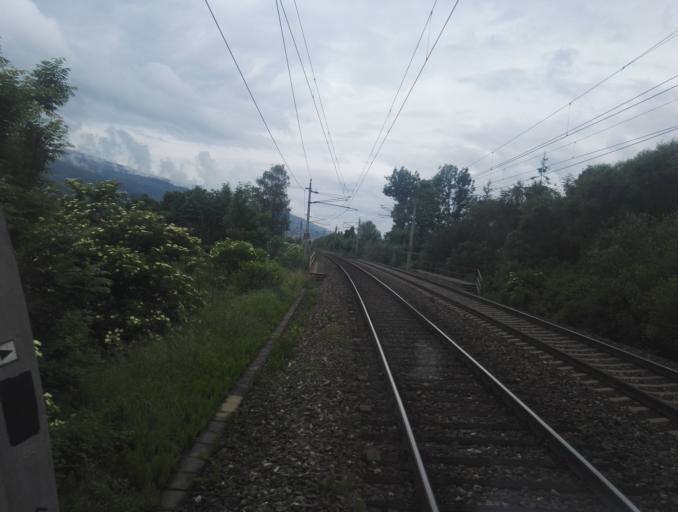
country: AT
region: Styria
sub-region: Politischer Bezirk Bruck-Muerzzuschlag
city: Mitterdorf im Muerztal
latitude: 47.5463
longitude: 15.5319
